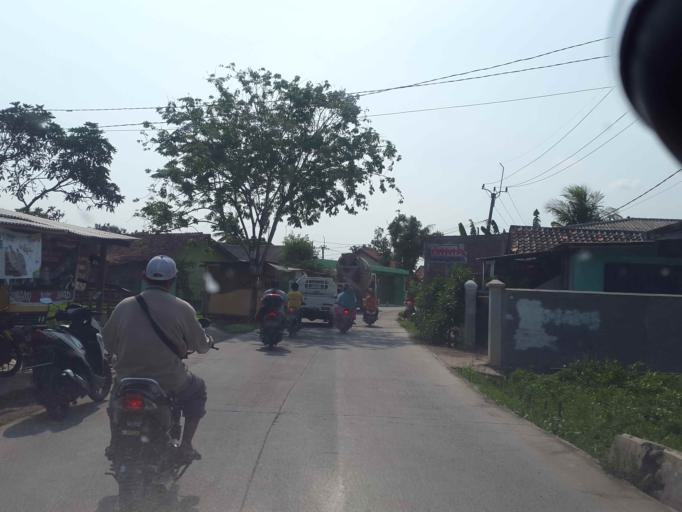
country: ID
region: West Java
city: Cikarang
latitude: -6.2172
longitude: 107.1603
